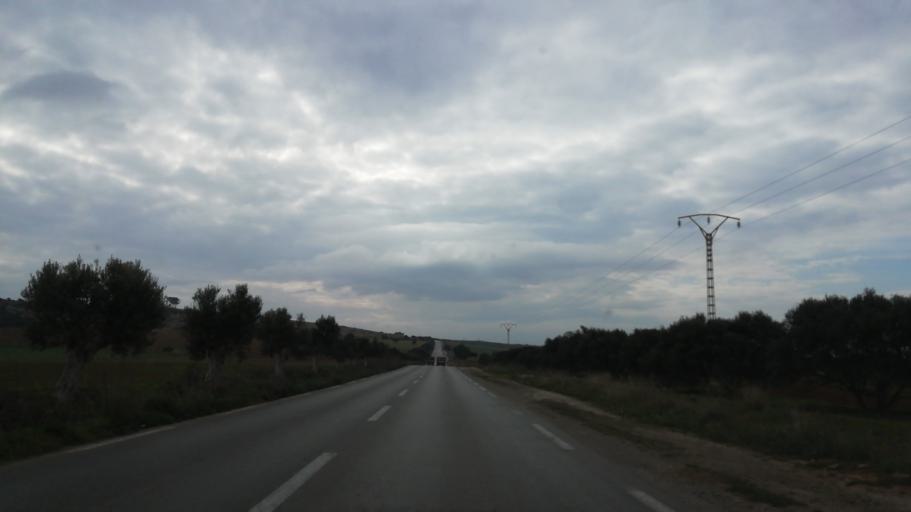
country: DZ
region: Oran
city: Ain el Bya
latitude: 35.7439
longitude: -0.3545
